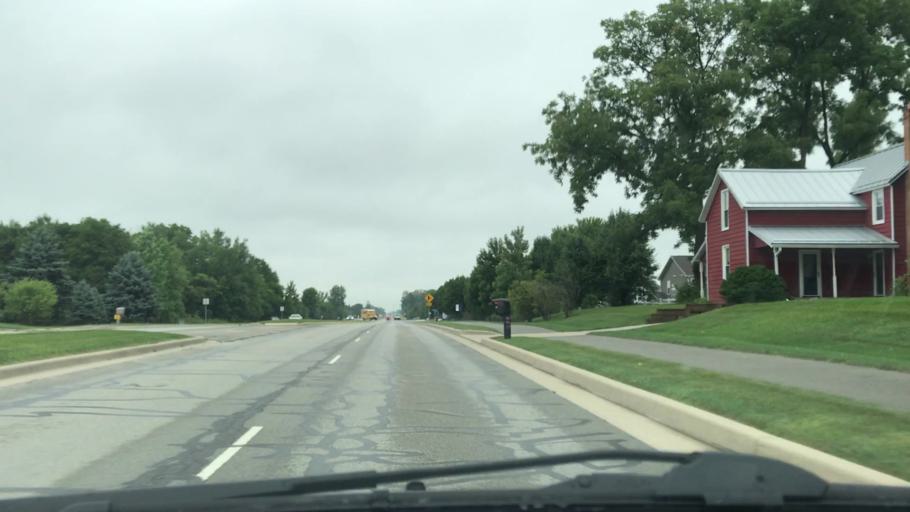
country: US
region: Indiana
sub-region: Hamilton County
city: Carmel
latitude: 40.0168
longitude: -86.0705
